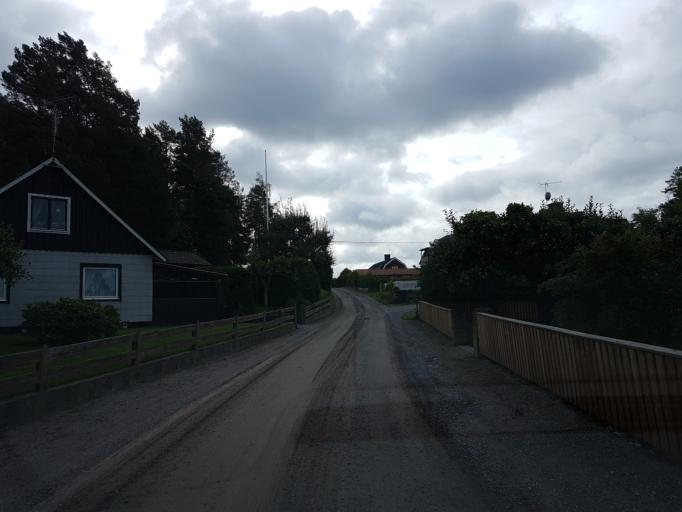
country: SE
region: OEstergoetland
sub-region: Atvidabergs Kommun
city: Atvidaberg
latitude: 58.2187
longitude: 16.0268
